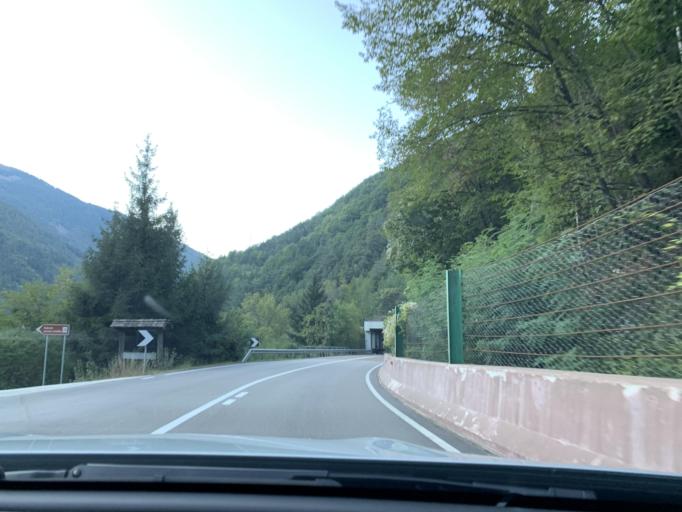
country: IT
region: Trentino-Alto Adige
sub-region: Bolzano
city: Cornedo All'Isarco
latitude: 46.4569
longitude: 11.4277
